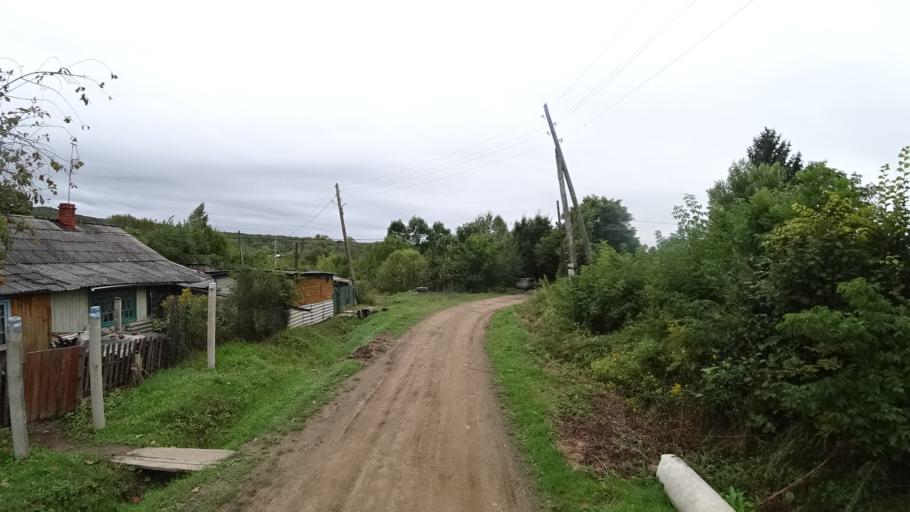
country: RU
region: Primorskiy
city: Rettikhovka
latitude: 44.1705
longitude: 132.7707
